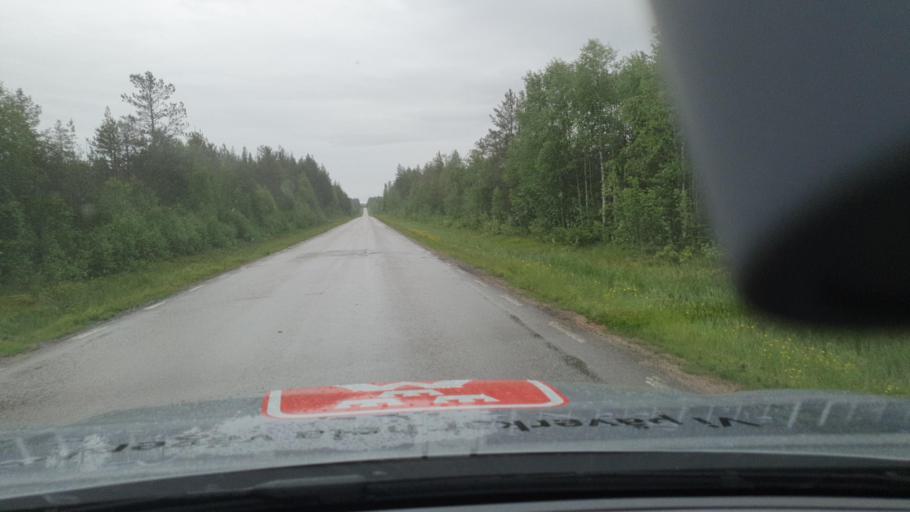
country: SE
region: Norrbotten
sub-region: Pajala Kommun
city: Pajala
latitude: 66.8377
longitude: 23.0893
